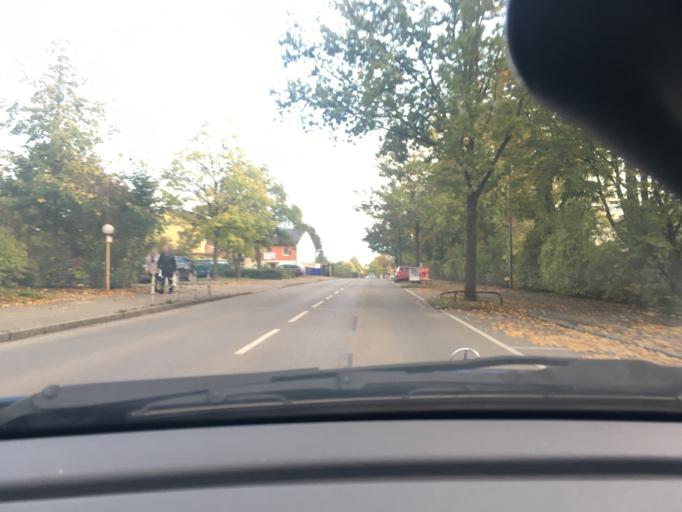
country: DE
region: Bavaria
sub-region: Swabia
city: Stadtbergen
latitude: 48.3998
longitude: 10.8230
